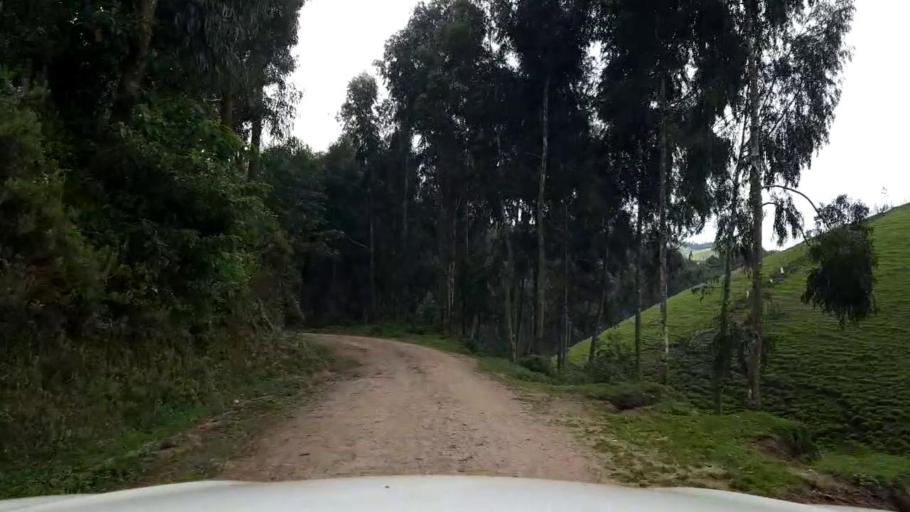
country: RW
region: Western Province
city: Gisenyi
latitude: -1.6844
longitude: 29.4174
